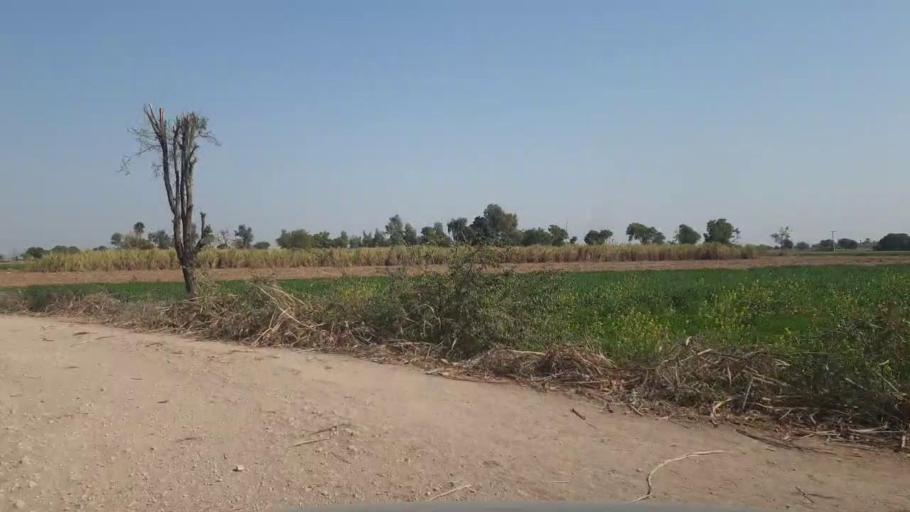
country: PK
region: Sindh
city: Chambar
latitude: 25.3126
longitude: 68.8742
